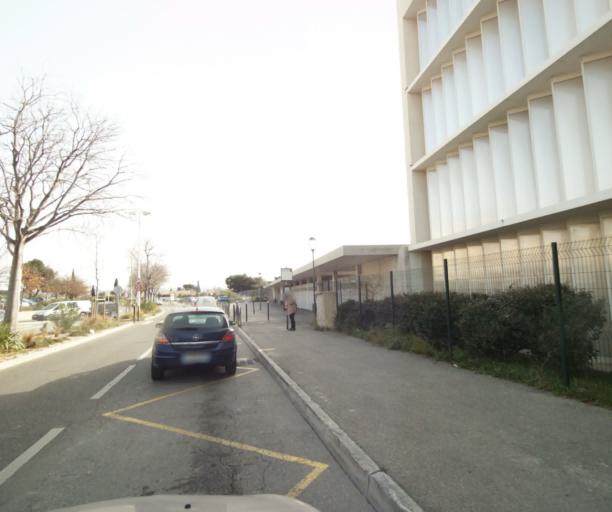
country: FR
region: Provence-Alpes-Cote d'Azur
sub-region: Departement des Bouches-du-Rhone
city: Vitrolles
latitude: 43.4475
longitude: 5.2471
